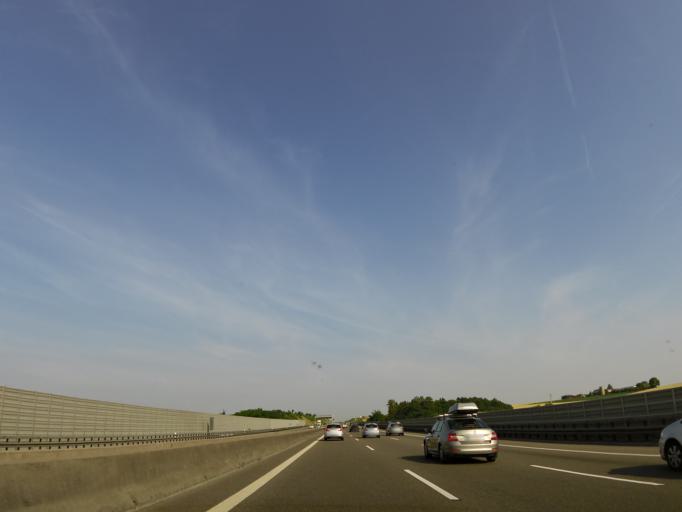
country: DE
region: Baden-Wuerttemberg
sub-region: Regierungsbezirk Stuttgart
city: Rutesheim
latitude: 48.7910
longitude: 8.9730
